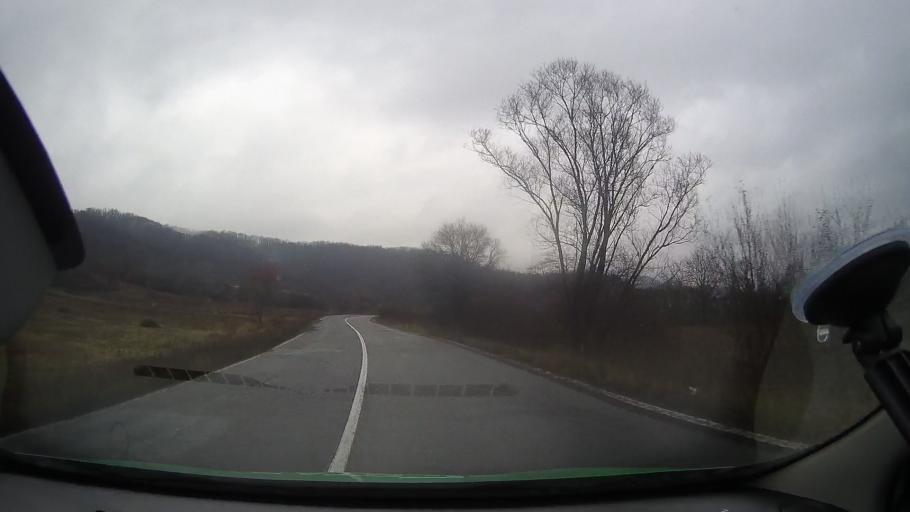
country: RO
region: Arad
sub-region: Comuna Gurahont
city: Gurahont
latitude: 46.2853
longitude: 22.3808
